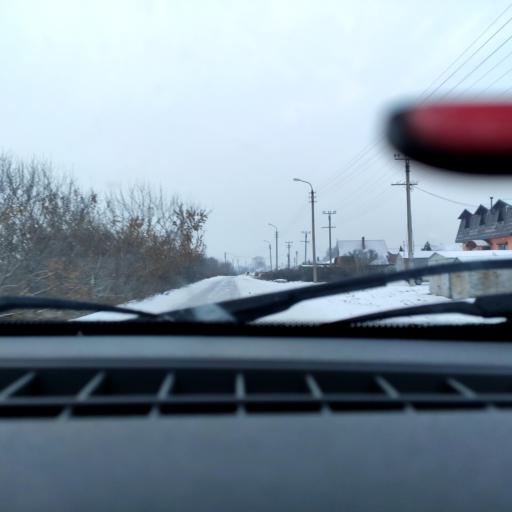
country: RU
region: Bashkortostan
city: Blagoveshchensk
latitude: 54.8951
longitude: 56.0265
